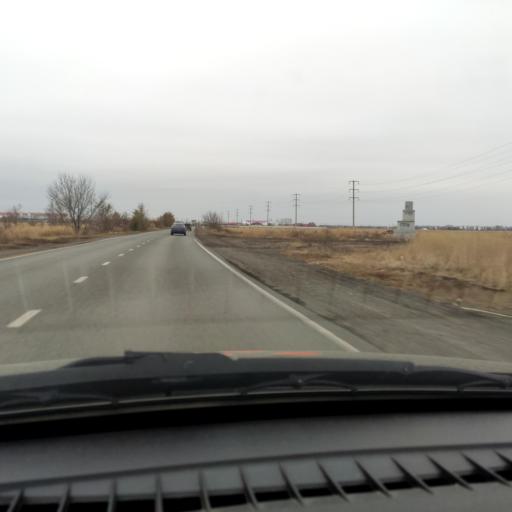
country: RU
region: Samara
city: Podstepki
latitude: 53.5195
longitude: 49.2058
